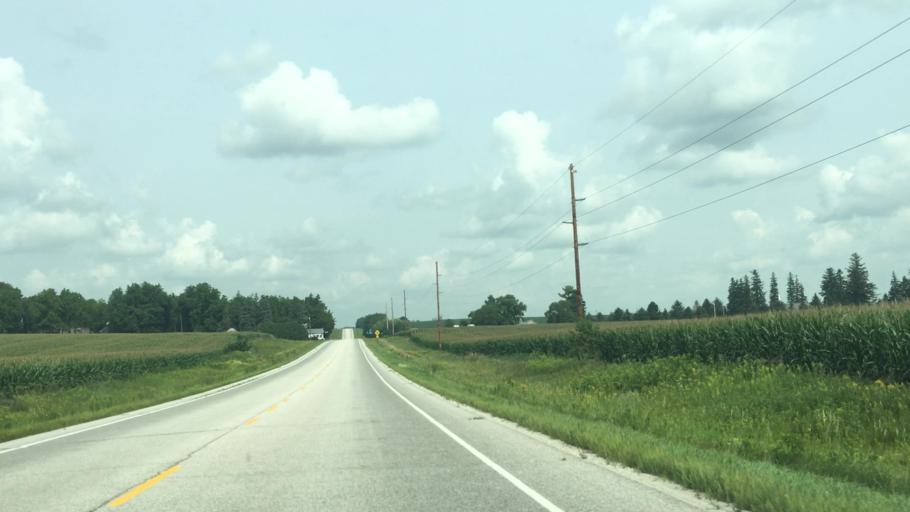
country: US
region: Minnesota
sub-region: Fillmore County
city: Harmony
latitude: 43.5907
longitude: -91.9298
